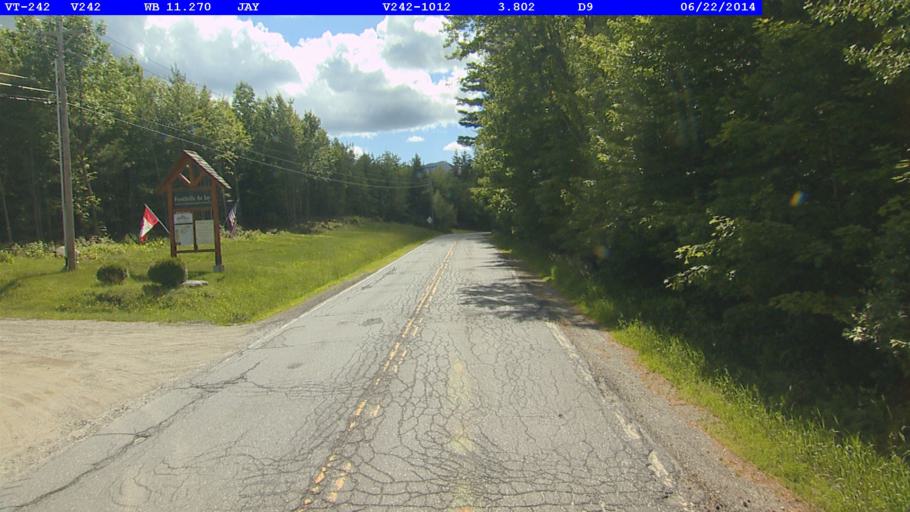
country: CA
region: Quebec
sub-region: Monteregie
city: Sutton
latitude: 44.9468
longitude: -72.4434
